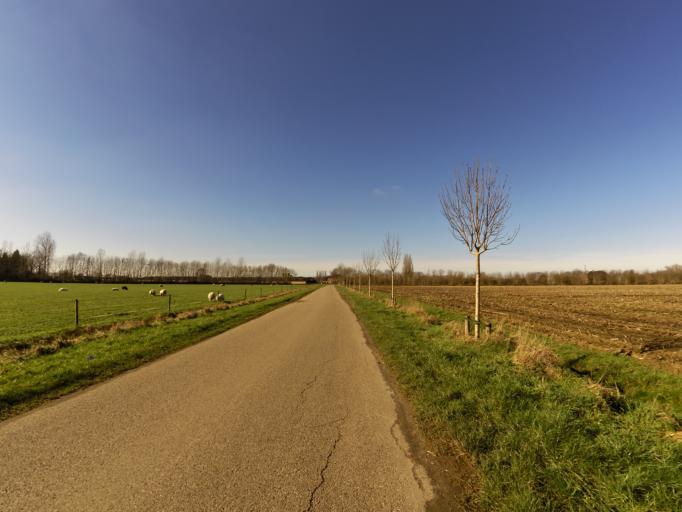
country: NL
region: Gelderland
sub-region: Gemeente Doetinchem
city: Doetinchem
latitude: 51.9515
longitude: 6.2495
